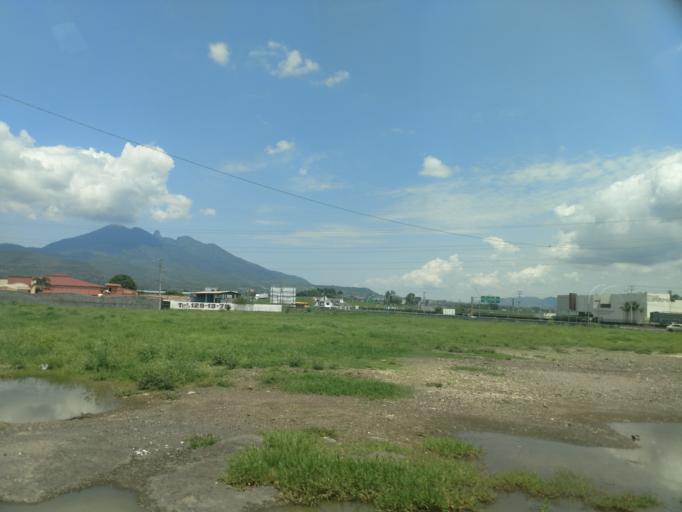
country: MX
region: Nayarit
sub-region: Tepic
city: La Corregidora
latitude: 21.4671
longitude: -104.8363
